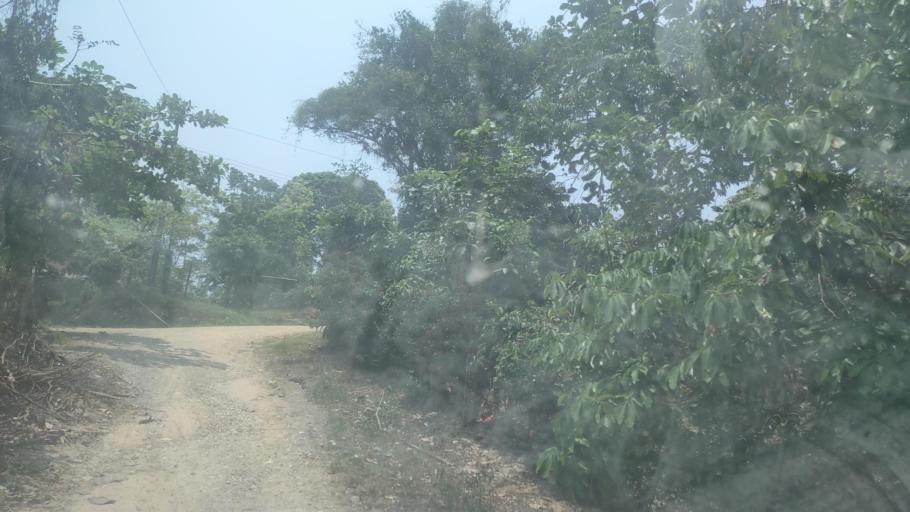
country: MX
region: Chiapas
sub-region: Tecpatan
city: Raudales Malpaso
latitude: 17.4587
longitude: -93.8001
